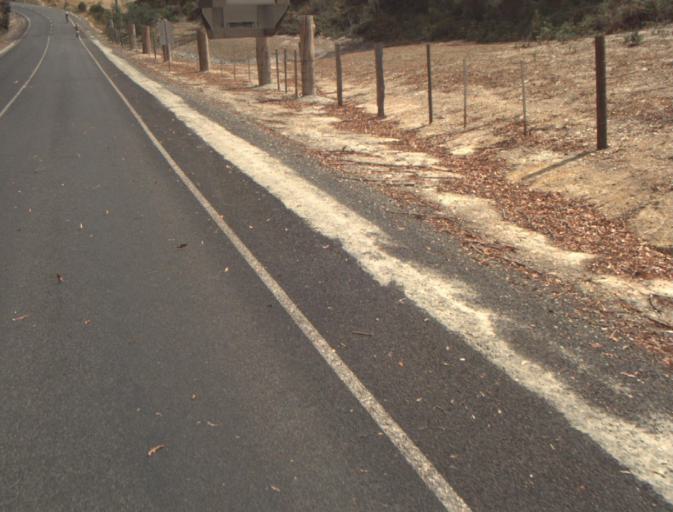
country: AU
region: Tasmania
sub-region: Dorset
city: Bridport
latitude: -41.1660
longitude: 147.2520
